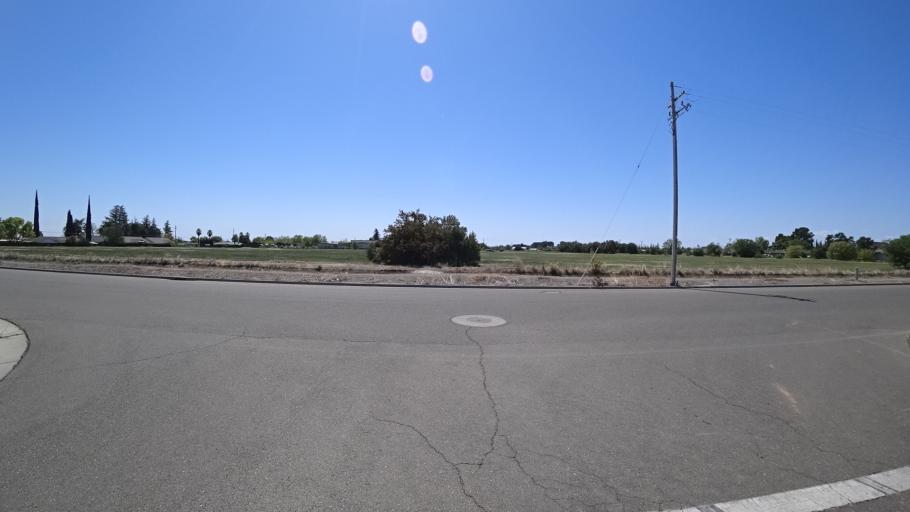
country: US
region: California
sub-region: Glenn County
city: Orland
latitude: 39.7510
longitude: -122.1757
